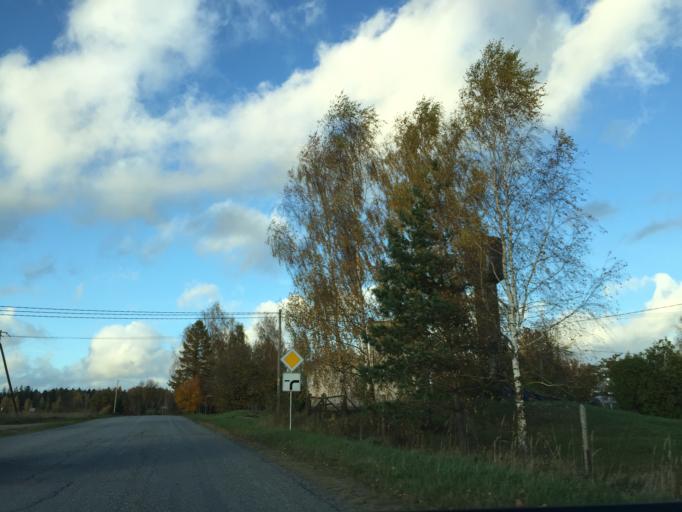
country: LV
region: Ogre
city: Jumprava
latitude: 56.7801
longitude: 25.0098
